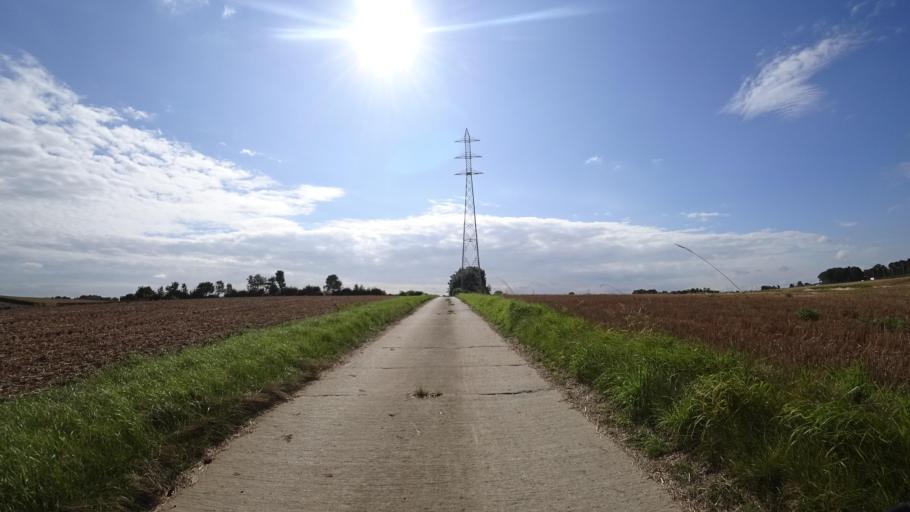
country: BE
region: Wallonia
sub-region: Province du Brabant Wallon
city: Louvain-la-Neuve
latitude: 50.6573
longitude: 4.6455
